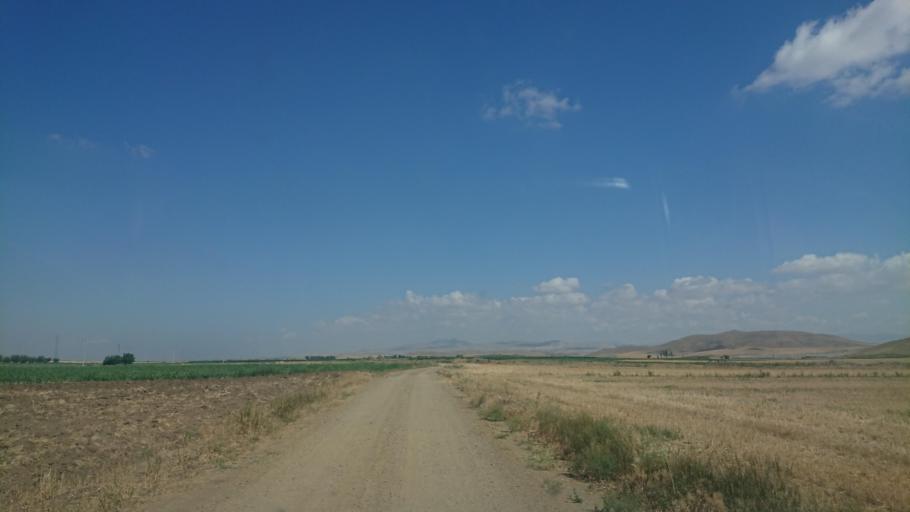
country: TR
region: Aksaray
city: Sariyahsi
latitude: 38.9801
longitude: 33.9096
